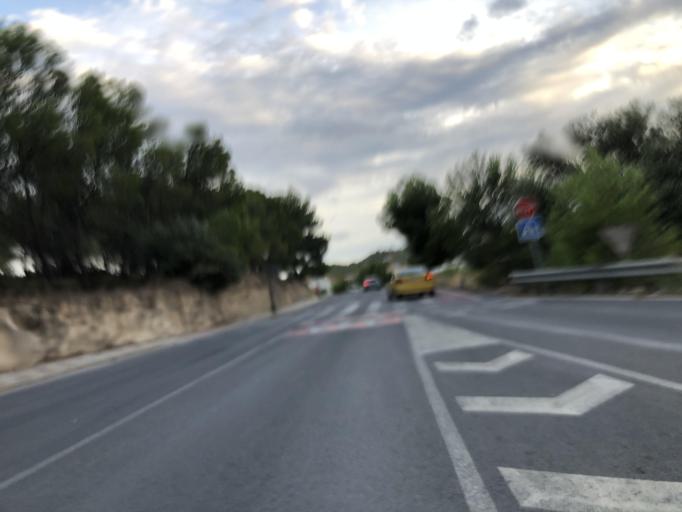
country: ES
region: Valencia
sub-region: Provincia de Alicante
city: Polop
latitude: 38.6256
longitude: -0.1359
